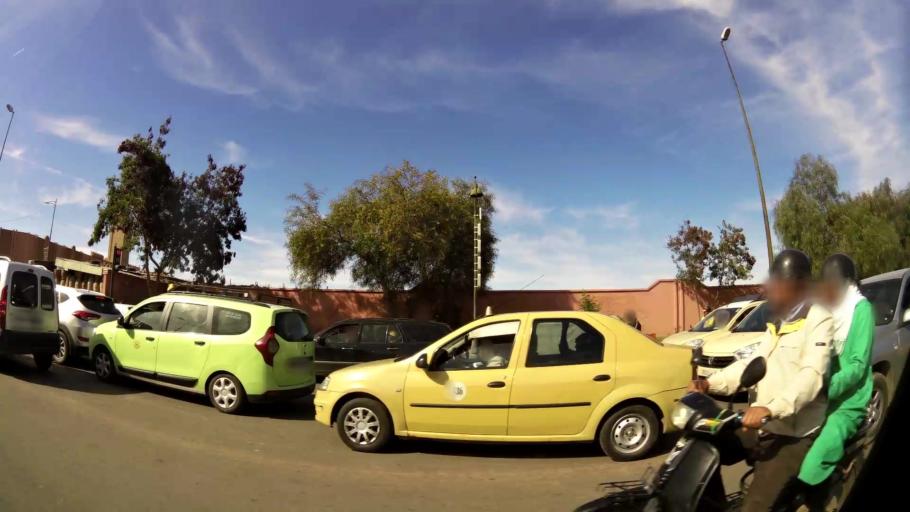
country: MA
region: Marrakech-Tensift-Al Haouz
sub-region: Marrakech
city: Marrakesh
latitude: 31.6225
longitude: -7.9704
